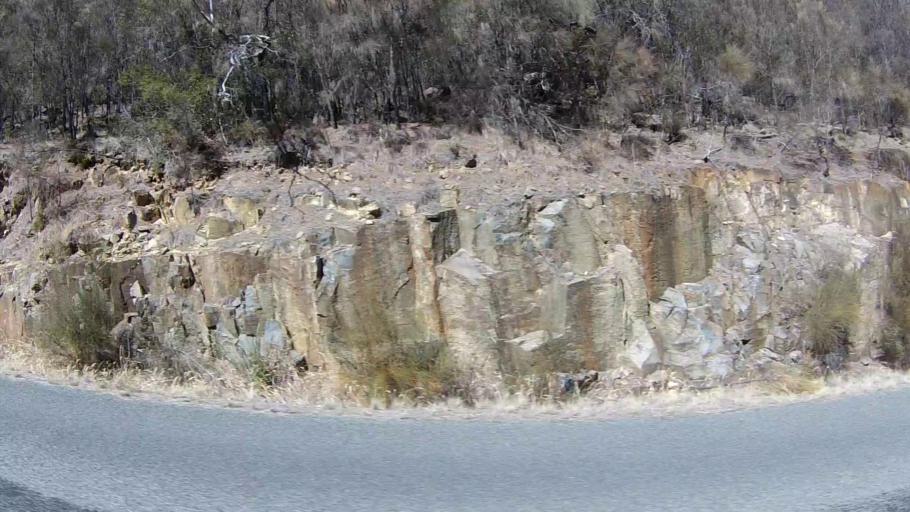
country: AU
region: Tasmania
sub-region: Sorell
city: Sorell
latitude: -42.5589
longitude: 147.8265
